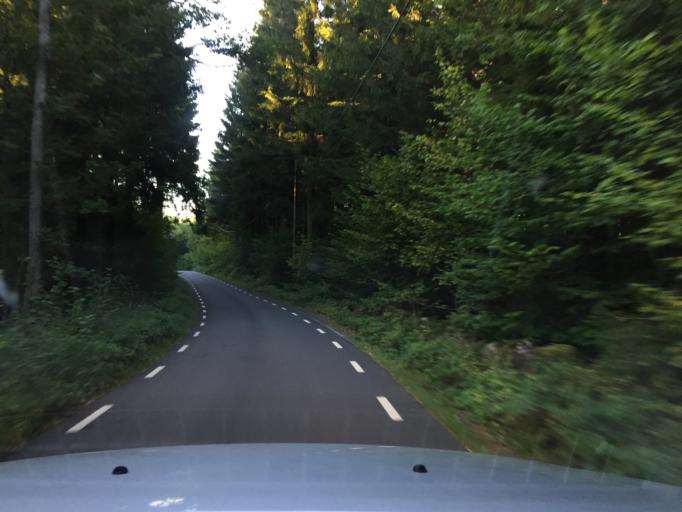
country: SE
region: Skane
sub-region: Hassleholms Kommun
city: Sosdala
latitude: 55.9762
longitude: 13.7453
